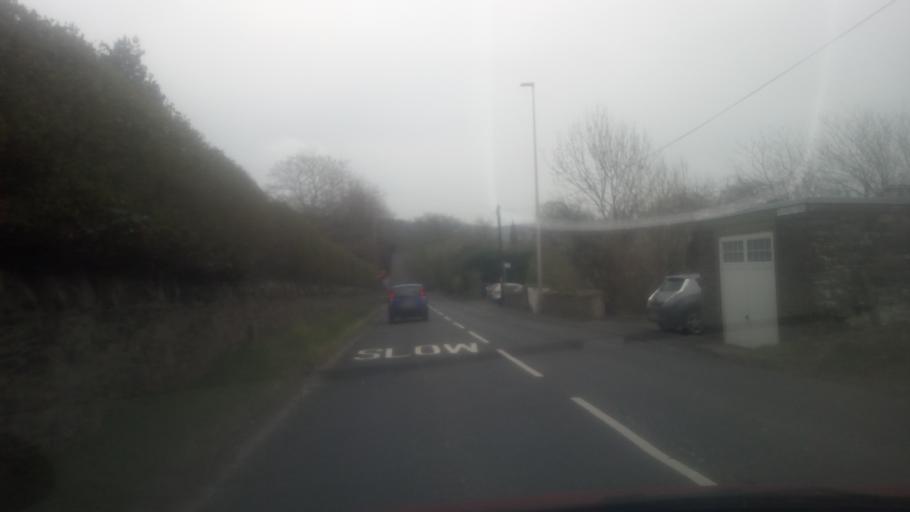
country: GB
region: Scotland
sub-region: The Scottish Borders
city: Galashiels
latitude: 55.6978
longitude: -2.8728
